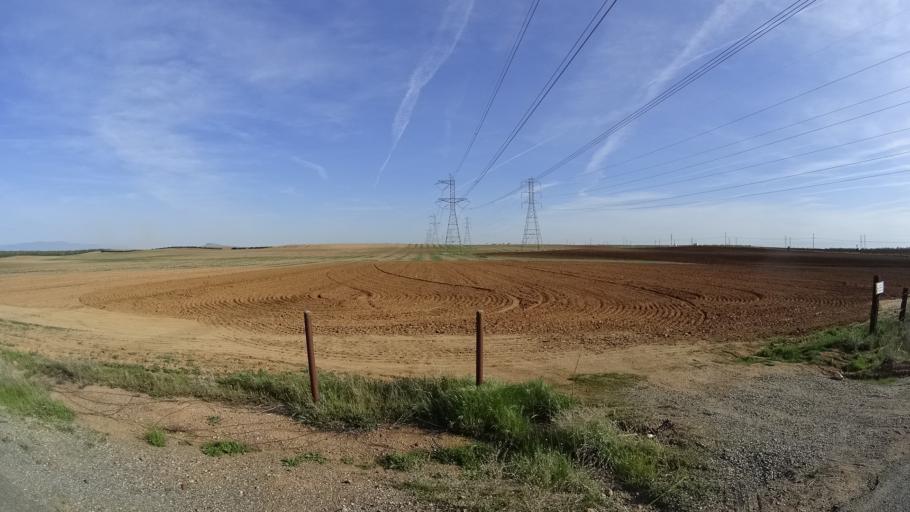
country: US
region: California
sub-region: Glenn County
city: Orland
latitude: 39.6684
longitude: -122.2741
